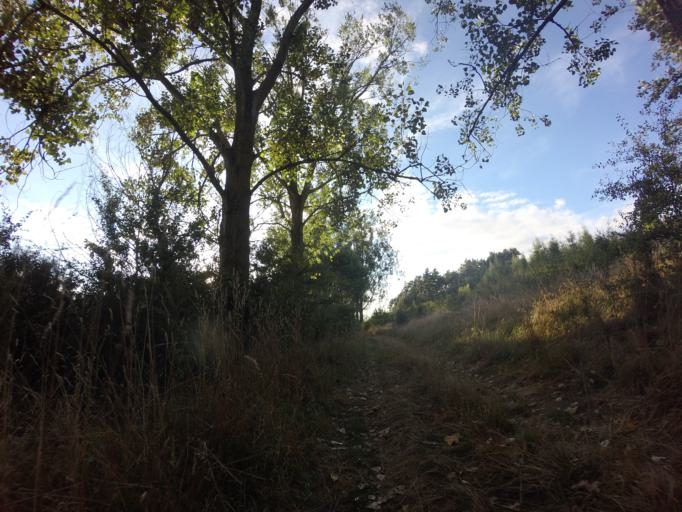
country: PL
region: West Pomeranian Voivodeship
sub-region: Powiat choszczenski
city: Choszczno
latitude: 53.1202
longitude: 15.4180
